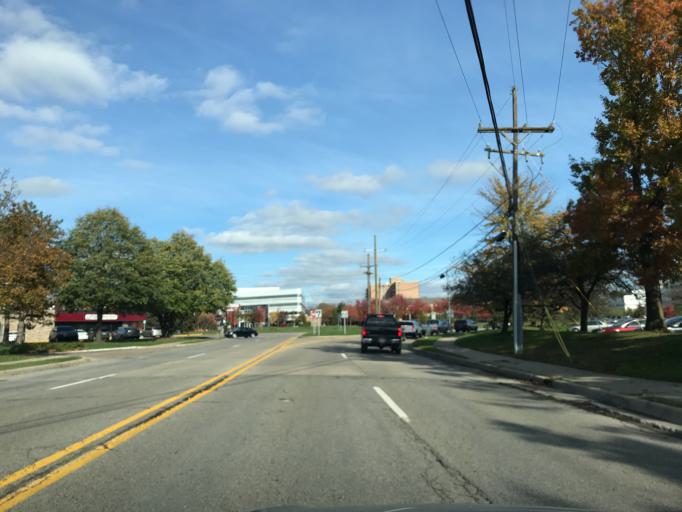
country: US
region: Michigan
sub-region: Oakland County
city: Franklin
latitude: 42.4958
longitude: -83.2999
